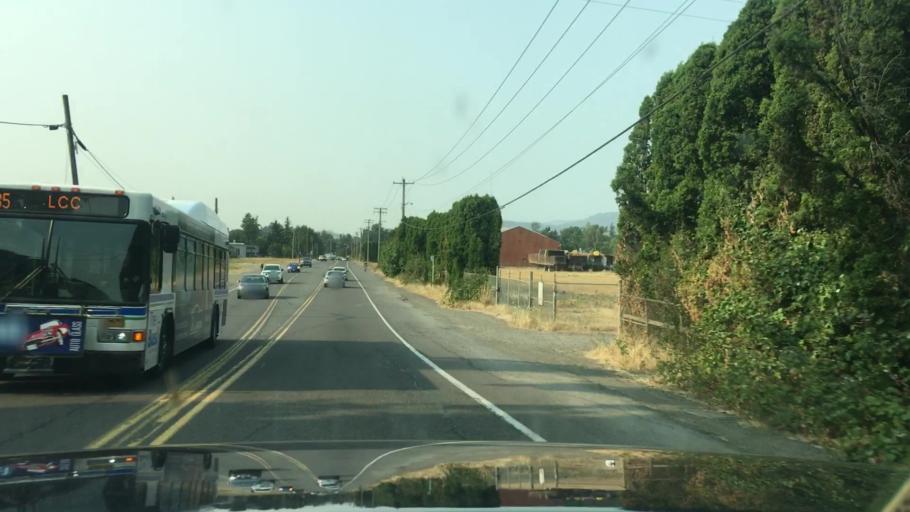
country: US
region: Oregon
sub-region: Lane County
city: Springfield
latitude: 44.0325
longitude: -123.0266
